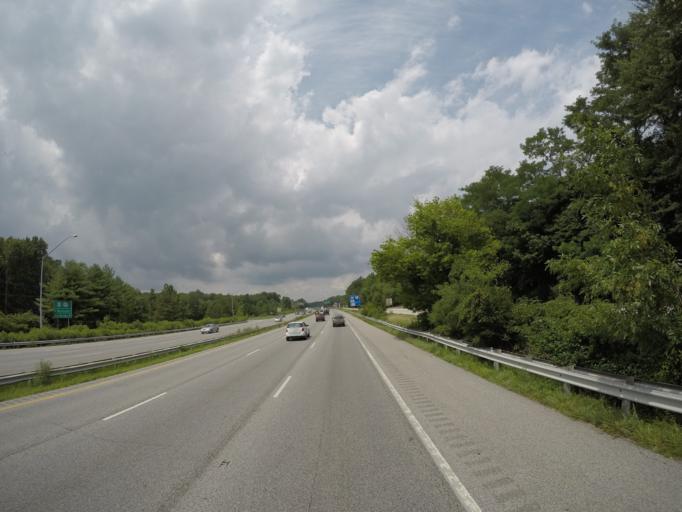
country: US
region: Maryland
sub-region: Anne Arundel County
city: Cape Saint Claire
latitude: 39.0258
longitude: -76.4373
